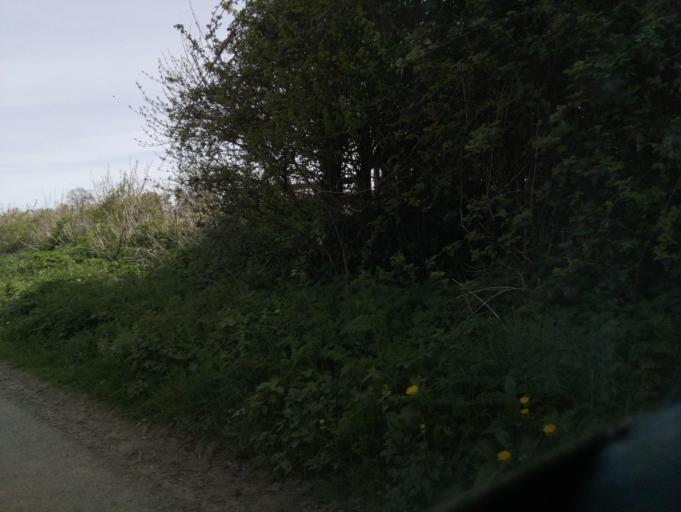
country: GB
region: England
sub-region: Dorset
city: Sherborne
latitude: 50.9925
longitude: -2.5442
